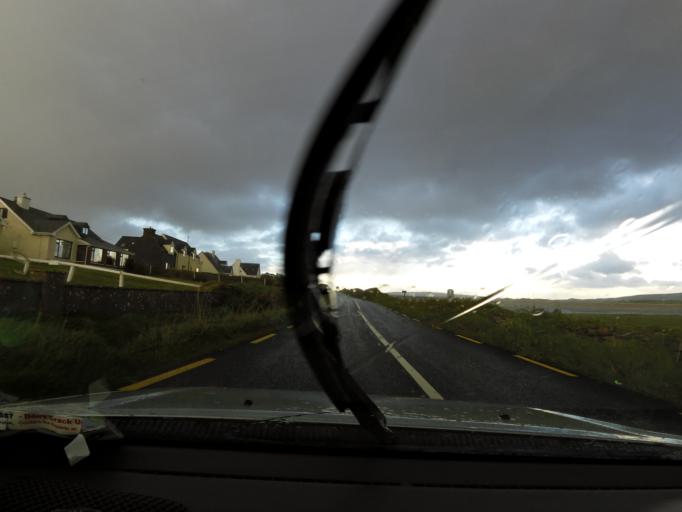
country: IE
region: Munster
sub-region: An Clar
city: Kilrush
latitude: 52.9472
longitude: -9.3583
